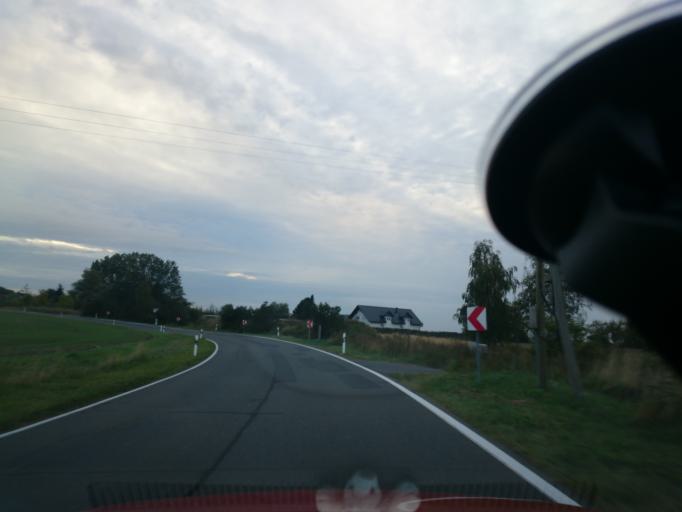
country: DE
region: Mecklenburg-Vorpommern
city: Saal
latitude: 54.3356
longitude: 12.5343
